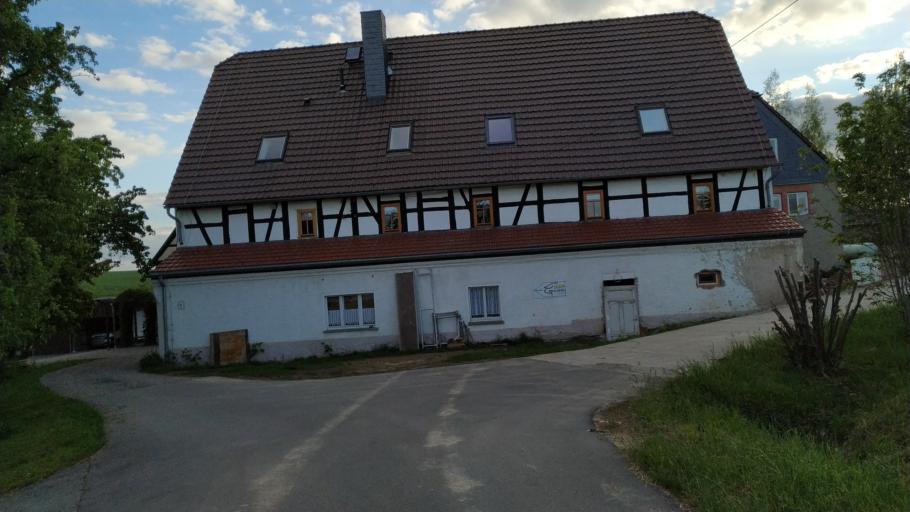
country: DE
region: Thuringia
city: Gopfersdorf
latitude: 50.9001
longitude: 12.6056
